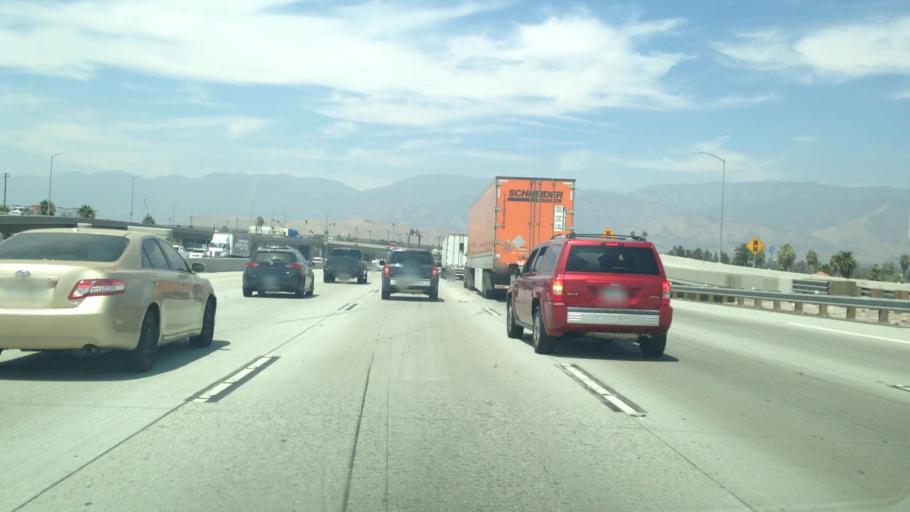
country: US
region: California
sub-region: San Bernardino County
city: San Bernardino
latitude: 34.1053
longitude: -117.3032
